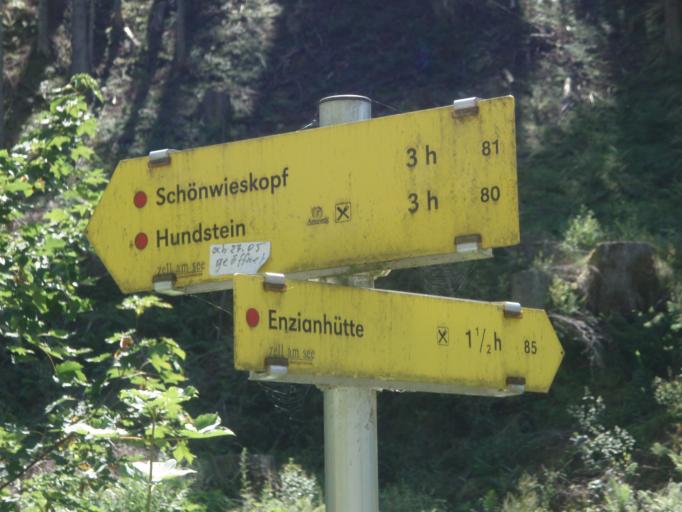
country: AT
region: Salzburg
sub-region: Politischer Bezirk Zell am See
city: Bruck an der Grossglocknerstrasse
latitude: 47.3346
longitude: 12.8626
